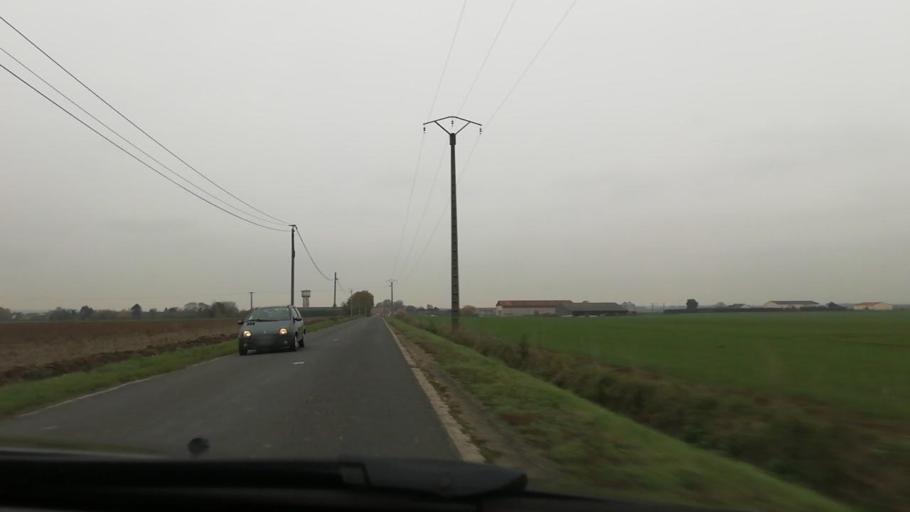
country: FR
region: Ile-de-France
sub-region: Departement de Seine-et-Marne
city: Claye-Souilly
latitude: 48.9682
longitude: 2.7138
